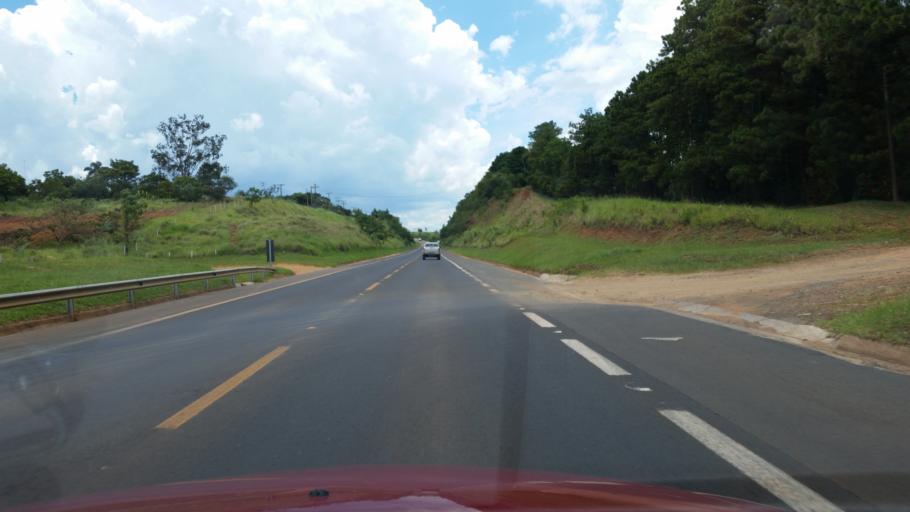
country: BR
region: Sao Paulo
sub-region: Itai
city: Itai
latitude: -23.2738
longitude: -49.0174
